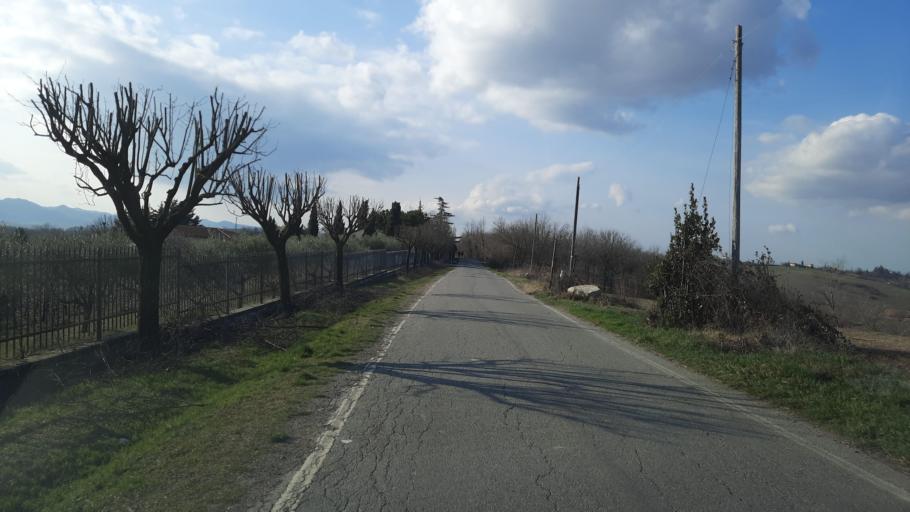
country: IT
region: Piedmont
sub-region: Provincia di Alessandria
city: San Giorgio
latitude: 45.1149
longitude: 8.4000
